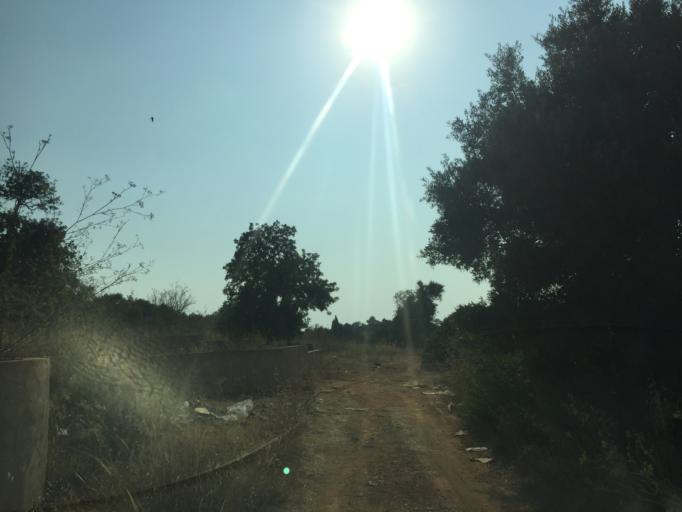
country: PT
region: Faro
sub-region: Albufeira
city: Guia
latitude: 37.0976
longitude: -8.2903
